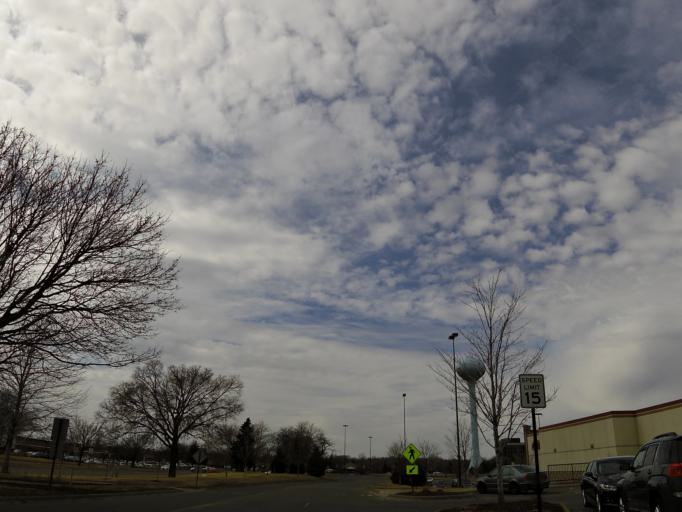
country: US
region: Minnesota
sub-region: Hennepin County
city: Edina
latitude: 44.8785
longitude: -93.3248
